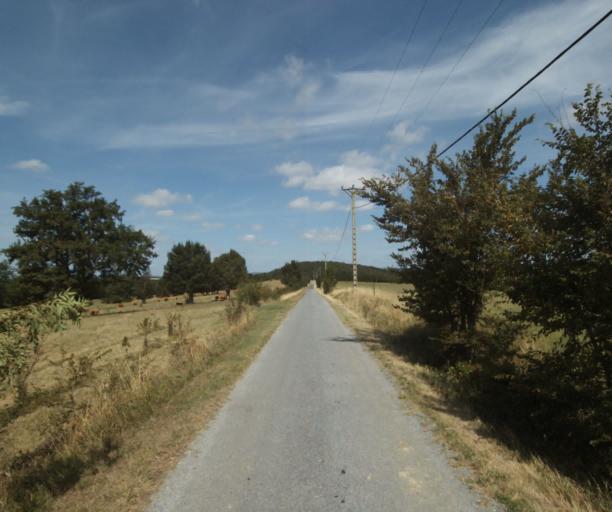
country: FR
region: Midi-Pyrenees
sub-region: Departement du Tarn
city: Dourgne
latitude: 43.4728
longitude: 2.1160
